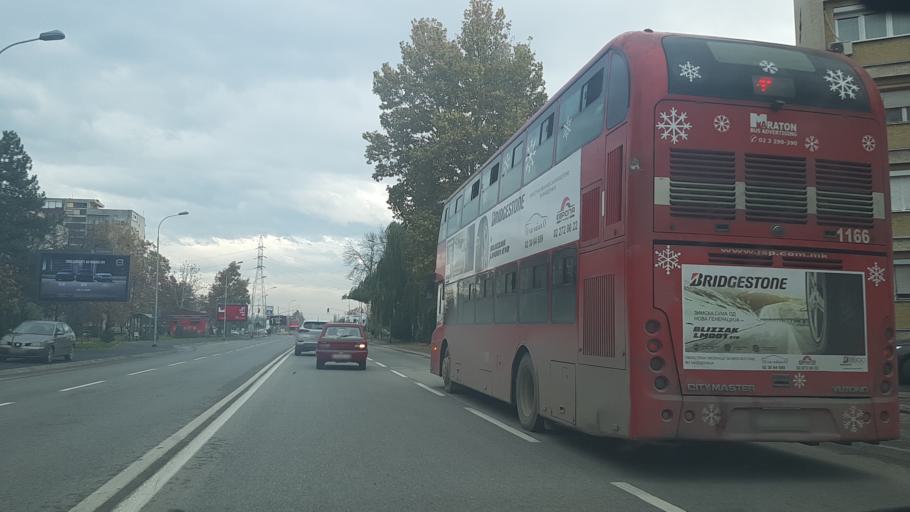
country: MK
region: Karpos
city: Skopje
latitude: 41.9792
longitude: 21.4447
